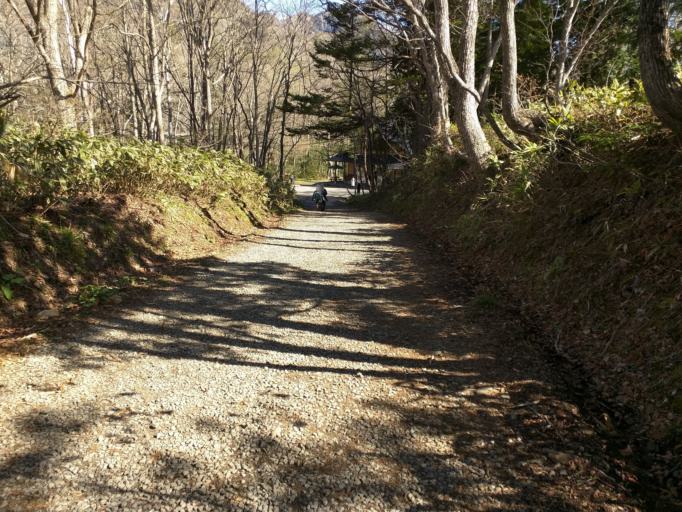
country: JP
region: Nagano
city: Nagano-shi
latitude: 36.7559
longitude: 138.0789
